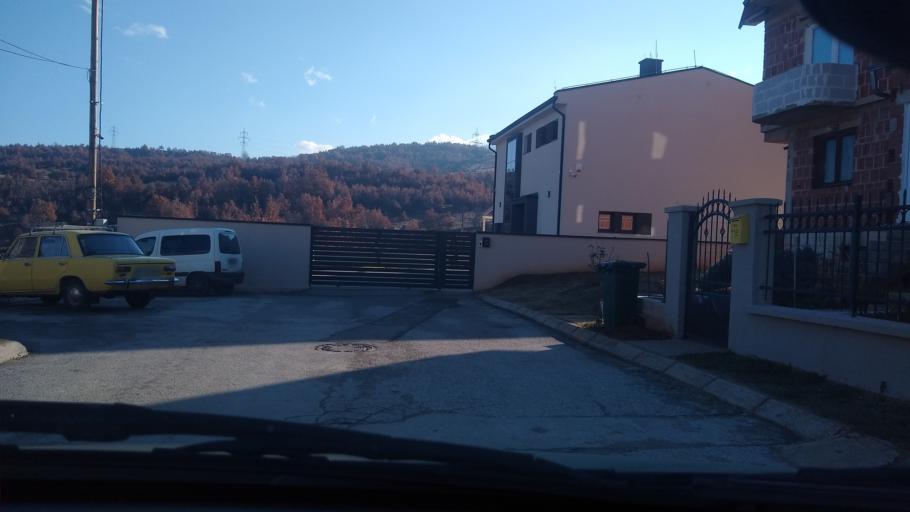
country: MK
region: Bitola
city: Bitola
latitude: 41.0172
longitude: 21.3146
